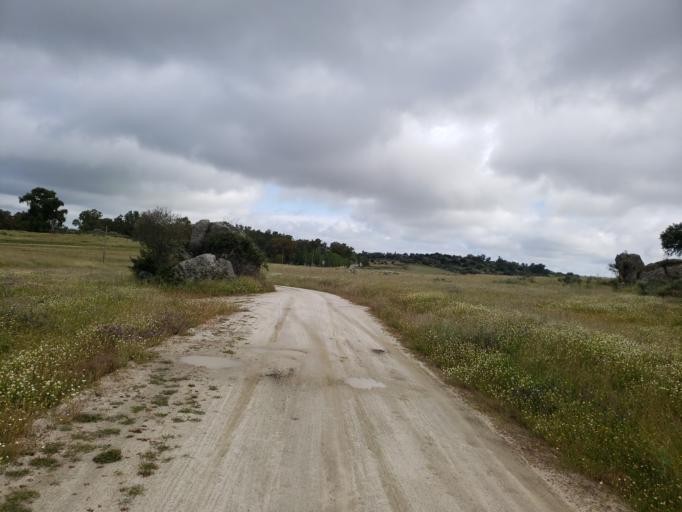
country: ES
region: Extremadura
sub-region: Provincia de Caceres
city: Malpartida de Caceres
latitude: 39.4255
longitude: -6.5035
